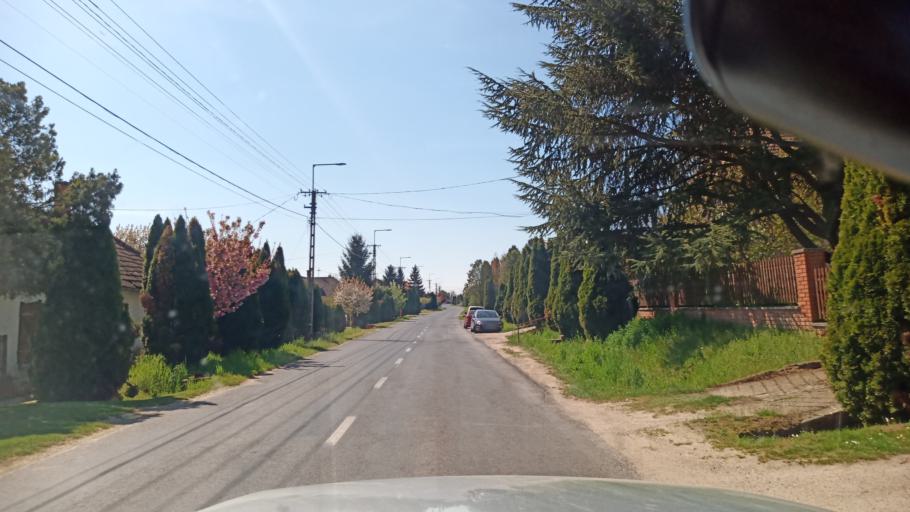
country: HU
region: Zala
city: Sarmellek
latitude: 46.7486
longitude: 17.1074
